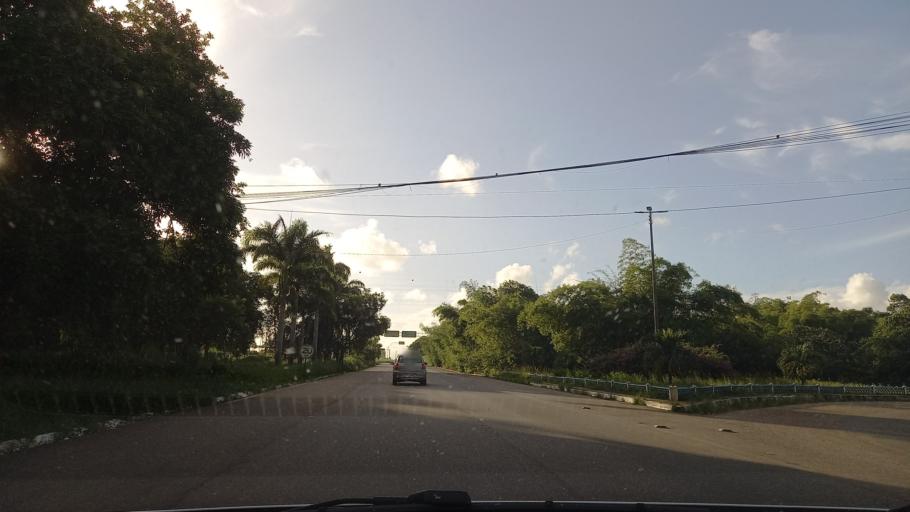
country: BR
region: Pernambuco
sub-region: Cabo De Santo Agostinho
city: Cabo
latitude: -8.3215
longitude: -35.0098
